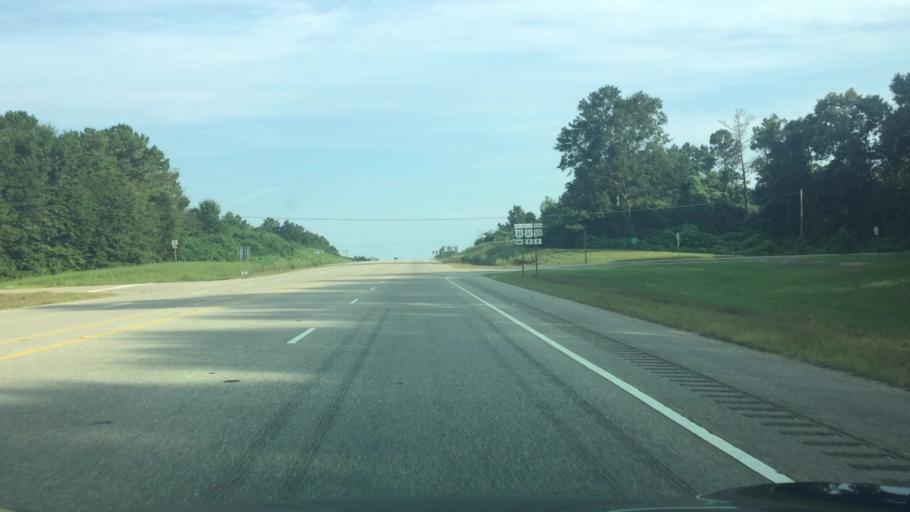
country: US
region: Alabama
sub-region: Butler County
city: Georgiana
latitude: 31.5375
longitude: -86.7261
